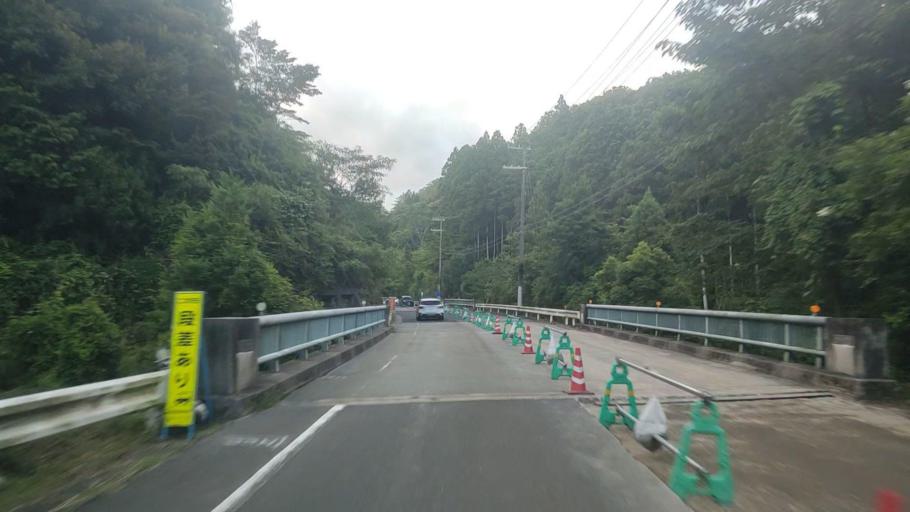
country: JP
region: Wakayama
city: Tanabe
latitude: 33.8309
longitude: 135.6508
